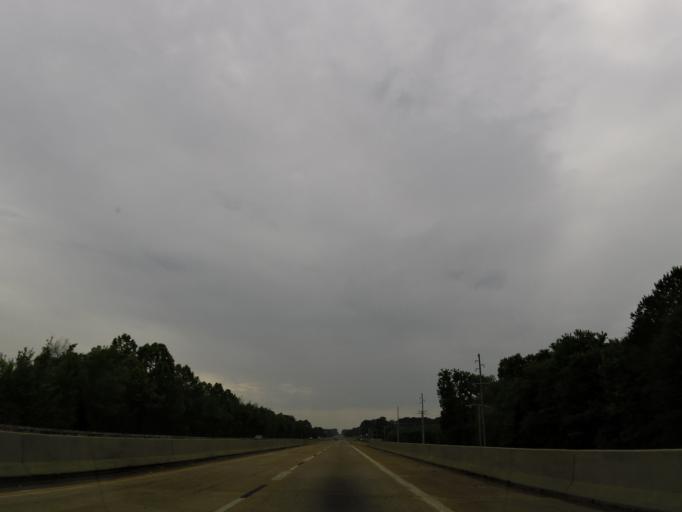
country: US
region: Alabama
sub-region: Madison County
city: Moores Mill
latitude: 34.7437
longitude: -86.4464
